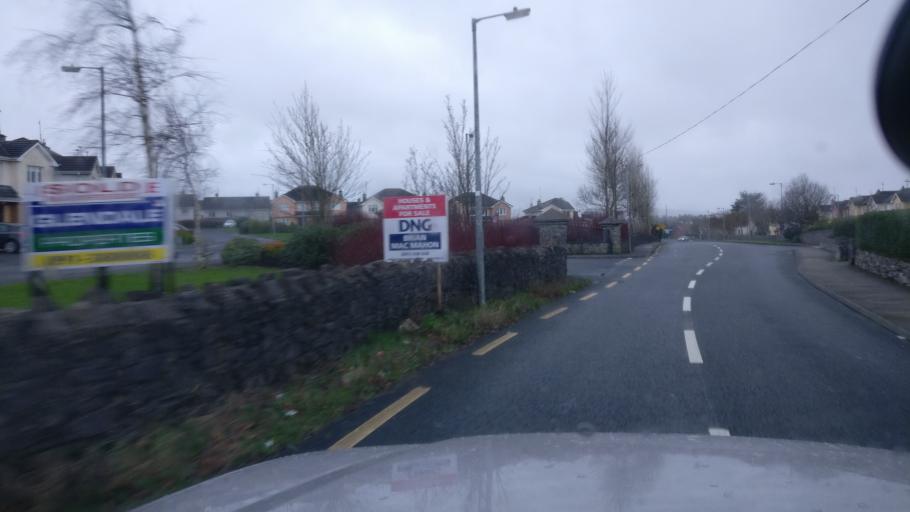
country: IE
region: Connaught
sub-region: County Galway
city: Loughrea
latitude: 53.2049
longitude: -8.5581
